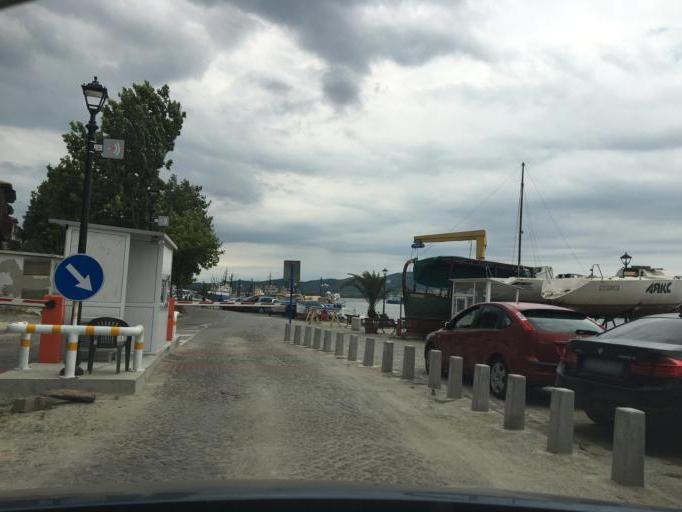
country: BG
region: Burgas
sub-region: Obshtina Sozopol
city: Sozopol
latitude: 42.4243
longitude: 27.6938
